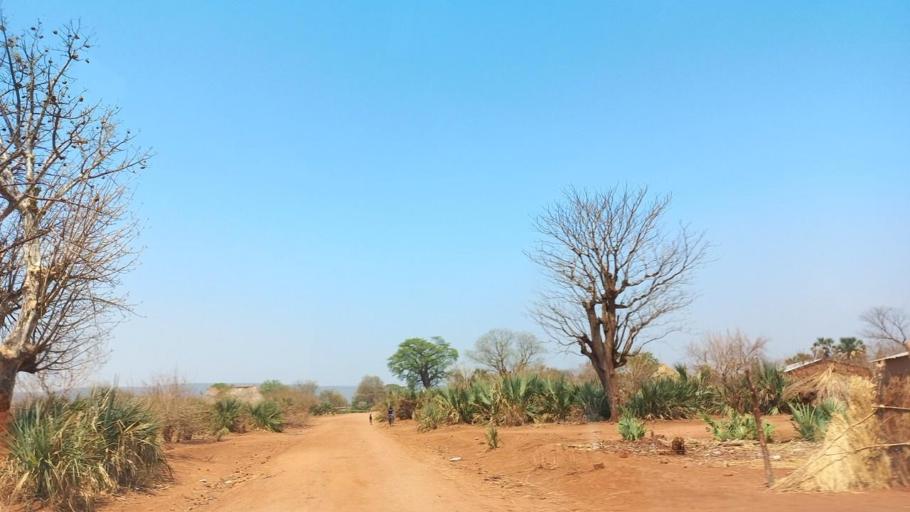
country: ZM
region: Lusaka
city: Luangwa
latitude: -15.1876
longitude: 30.2062
